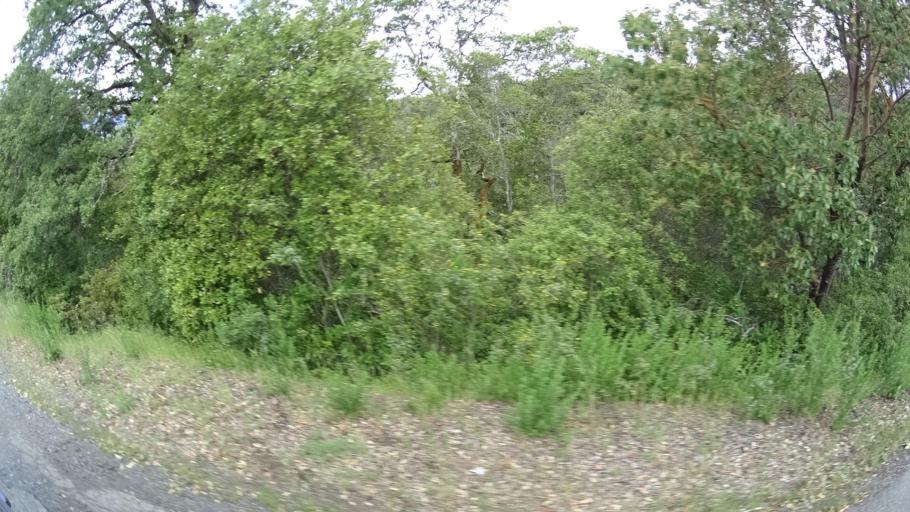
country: US
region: California
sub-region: Humboldt County
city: Redway
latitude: 40.1809
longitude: -123.5930
